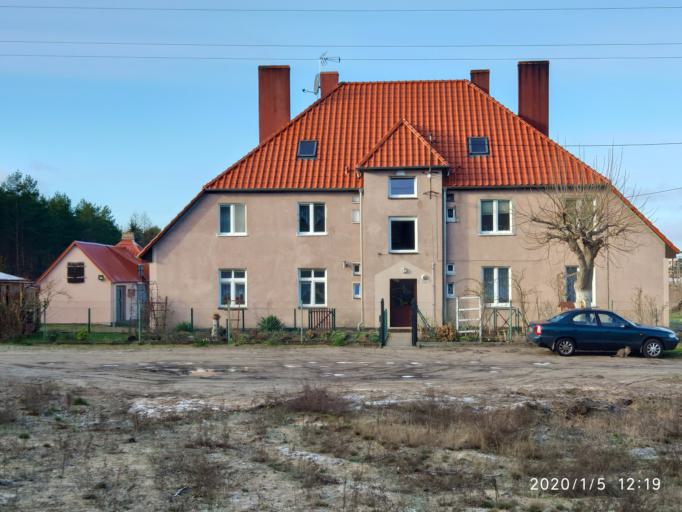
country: PL
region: Lubusz
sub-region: Powiat zielonogorski
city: Czerwiensk
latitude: 52.0152
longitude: 15.4031
